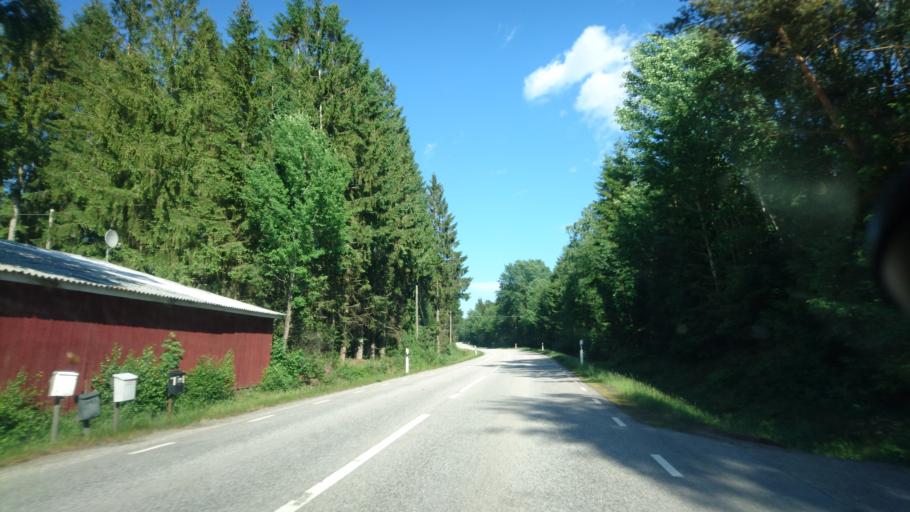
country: SE
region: Skane
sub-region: Osby Kommun
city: Lonsboda
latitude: 56.3916
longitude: 14.4354
